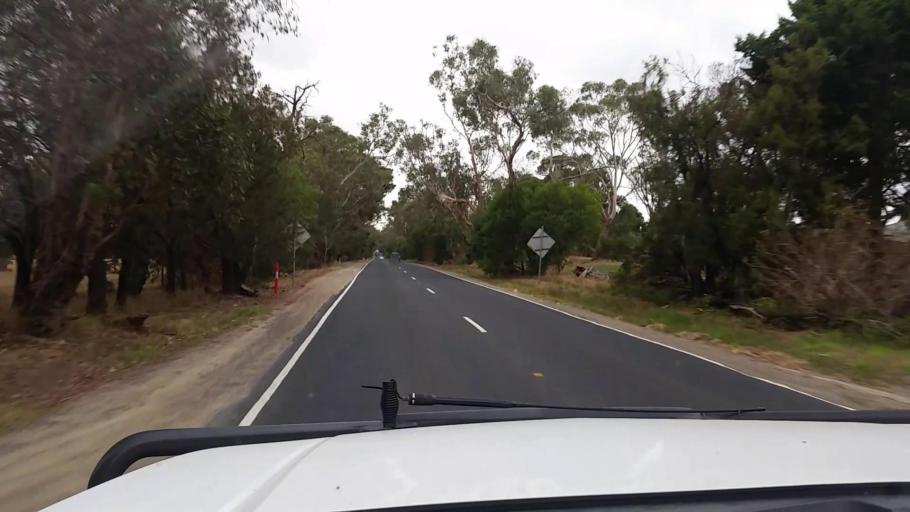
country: AU
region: Victoria
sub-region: Mornington Peninsula
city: Somerville
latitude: -38.2331
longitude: 145.1518
